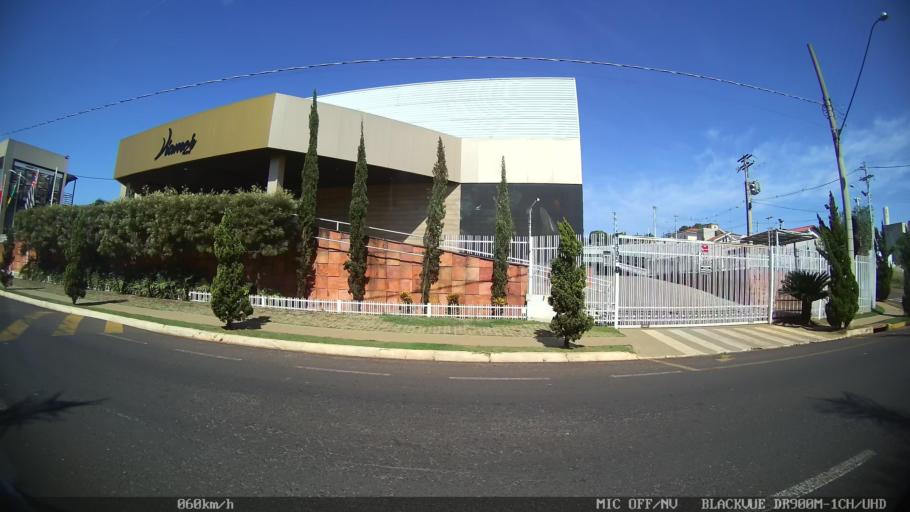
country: BR
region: Sao Paulo
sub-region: Sao Jose Do Rio Preto
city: Sao Jose do Rio Preto
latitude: -20.7783
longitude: -49.3897
